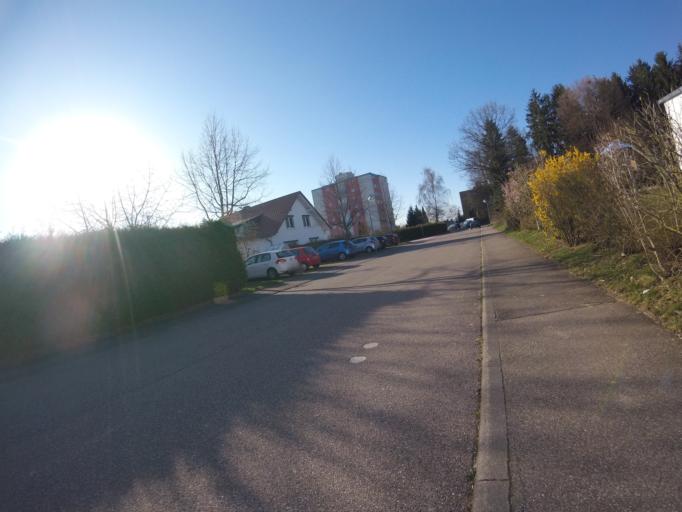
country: DE
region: Baden-Wuerttemberg
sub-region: Regierungsbezirk Stuttgart
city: Durlangen
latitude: 48.8621
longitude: 9.7887
